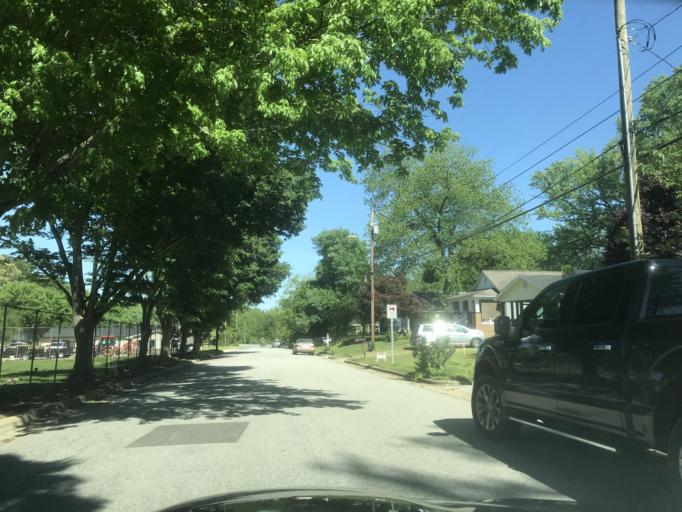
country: US
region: North Carolina
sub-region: Wake County
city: Raleigh
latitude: 35.7629
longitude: -78.6465
